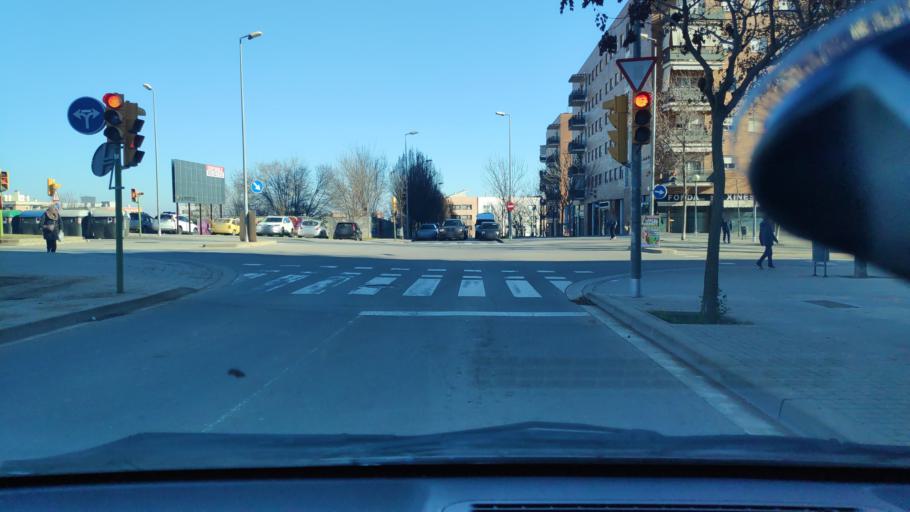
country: ES
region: Catalonia
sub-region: Provincia de Barcelona
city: Sant Quirze del Valles
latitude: 41.5631
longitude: 2.0816
